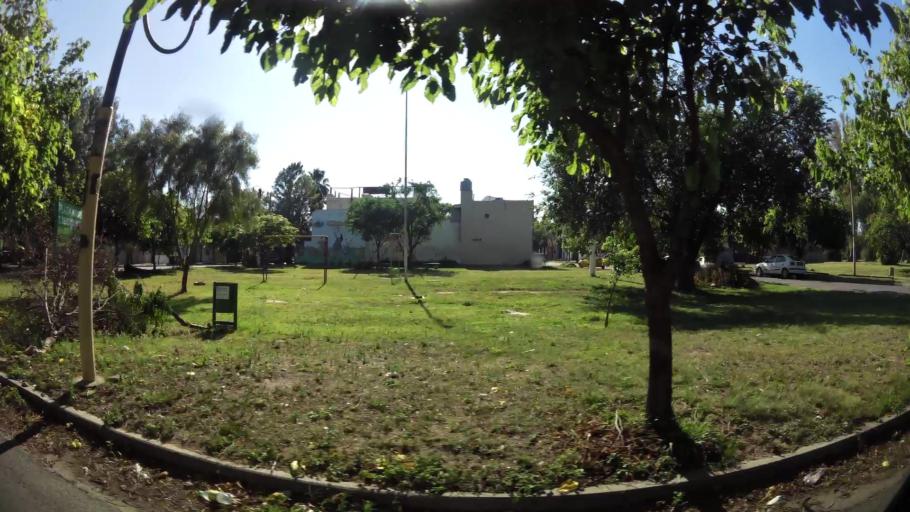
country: AR
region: Cordoba
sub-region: Departamento de Capital
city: Cordoba
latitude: -31.4191
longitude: -64.1575
